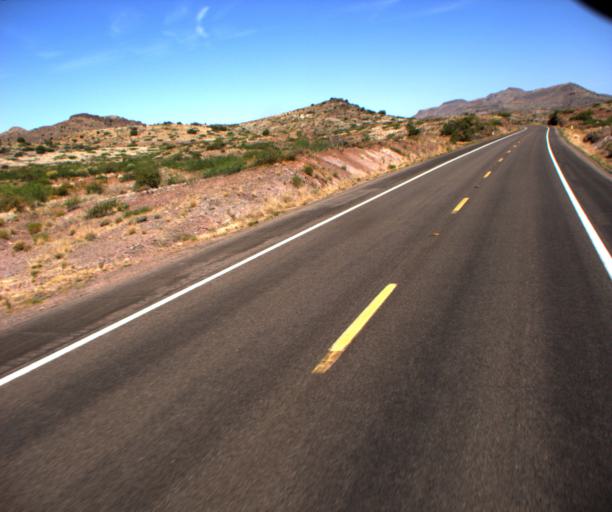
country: US
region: Arizona
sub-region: Greenlee County
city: Clifton
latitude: 32.7636
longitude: -109.2503
